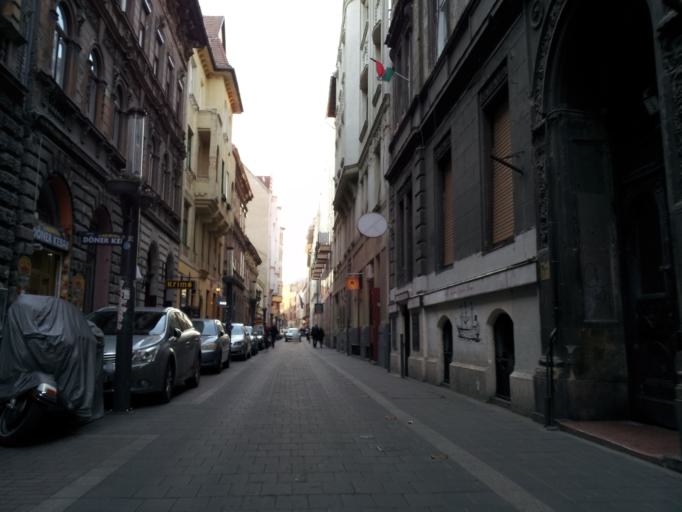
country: HU
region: Budapest
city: Budapest VII. keruelet
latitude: 47.4964
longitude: 19.0639
